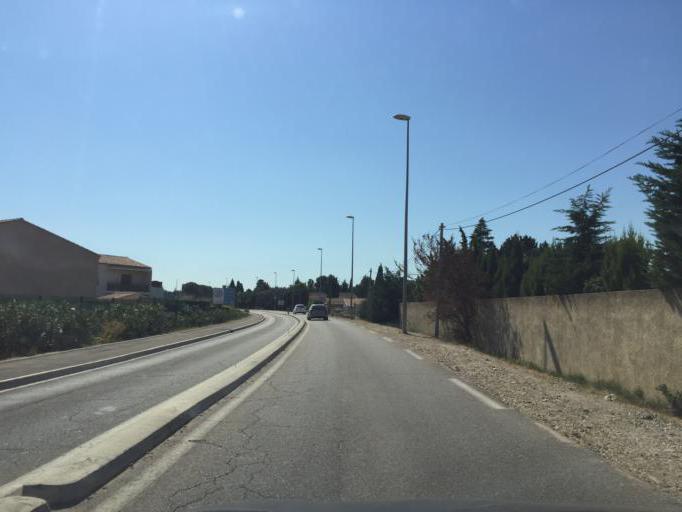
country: FR
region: Provence-Alpes-Cote d'Azur
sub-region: Departement du Vaucluse
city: Vedene
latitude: 43.9755
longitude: 4.9097
